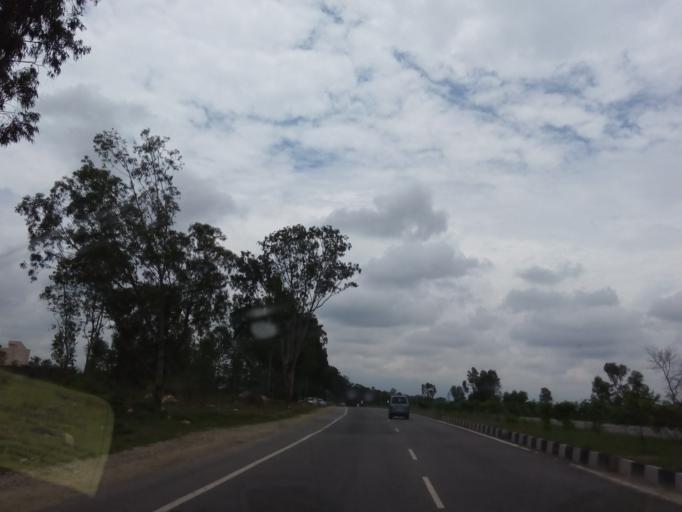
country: IN
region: Karnataka
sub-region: Hassan
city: Channarayapatna
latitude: 12.9742
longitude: 76.2722
